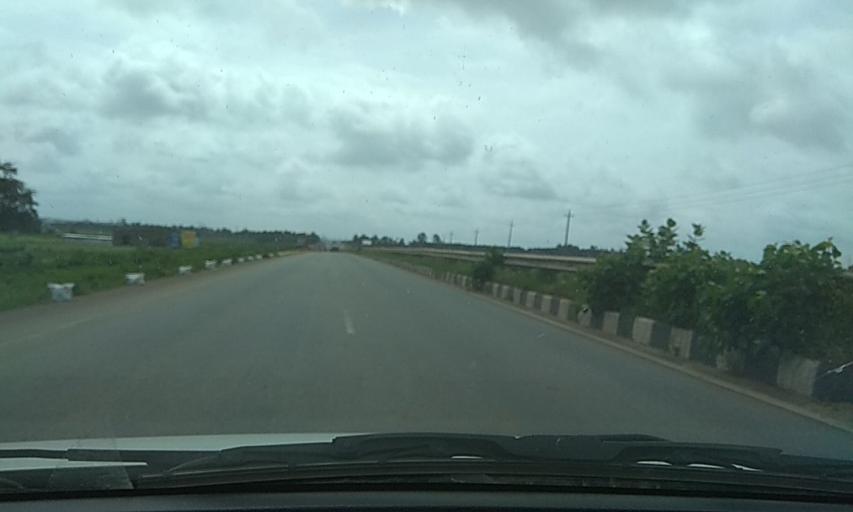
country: IN
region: Karnataka
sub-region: Davanagere
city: Harihar
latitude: 14.4505
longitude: 75.8781
